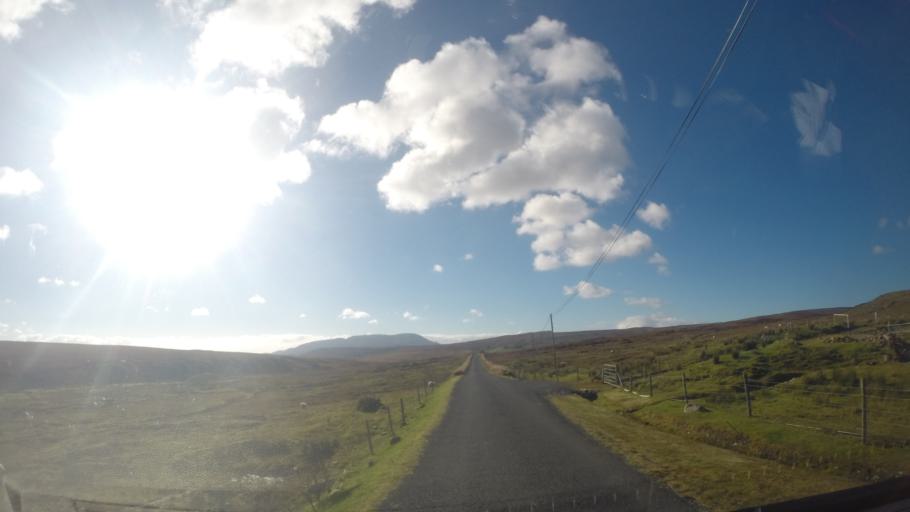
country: IE
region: Ulster
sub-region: County Donegal
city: Killybegs
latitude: 54.7177
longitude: -8.5884
